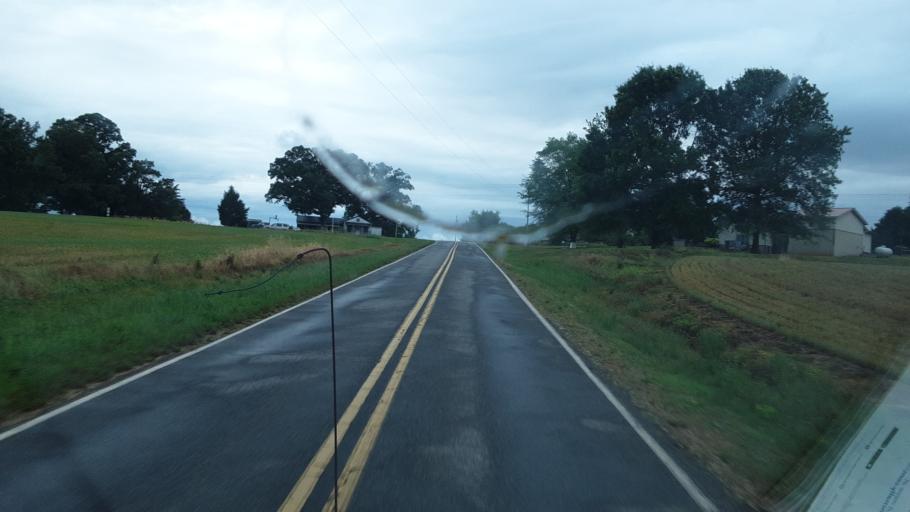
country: US
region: North Carolina
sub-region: Yadkin County
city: Jonesville
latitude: 36.0544
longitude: -80.8298
